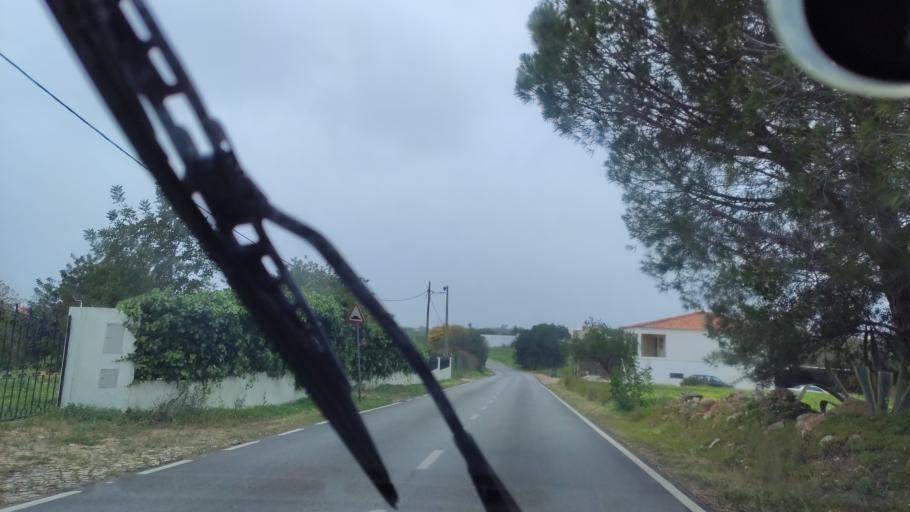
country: PT
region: Faro
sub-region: Faro
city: Santa Barbara de Nexe
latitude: 37.0768
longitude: -7.9563
